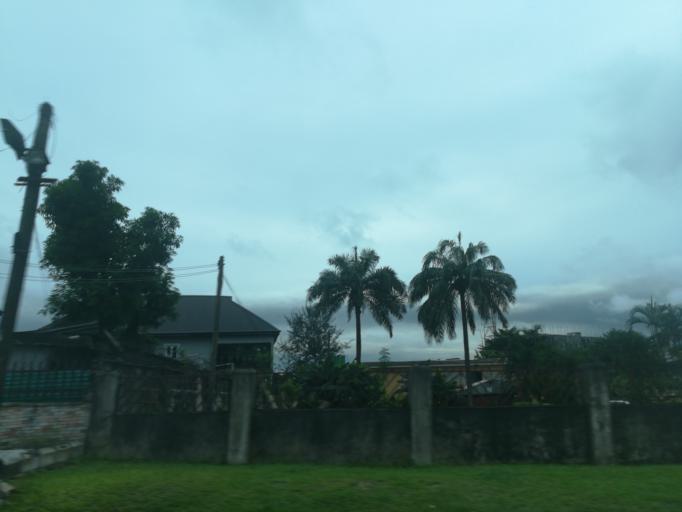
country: NG
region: Rivers
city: Port Harcourt
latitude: 4.8204
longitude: 6.9988
